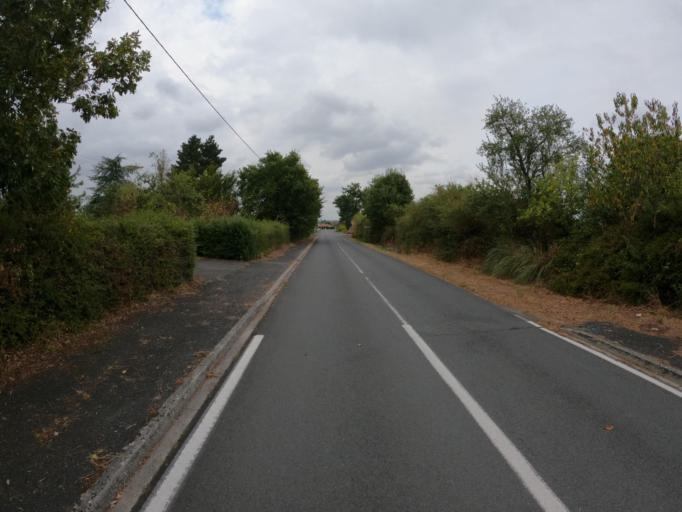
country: FR
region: Pays de la Loire
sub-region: Departement de Maine-et-Loire
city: La Romagne
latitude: 47.0567
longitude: -1.0261
